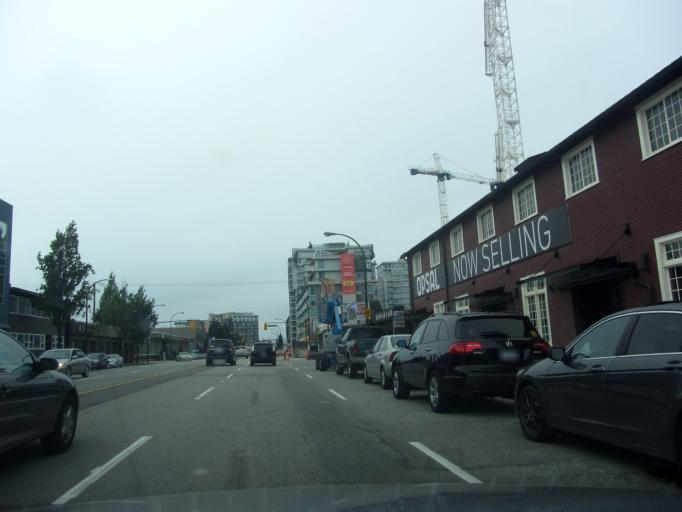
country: CA
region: British Columbia
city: Vancouver
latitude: 49.2614
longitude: -123.0979
